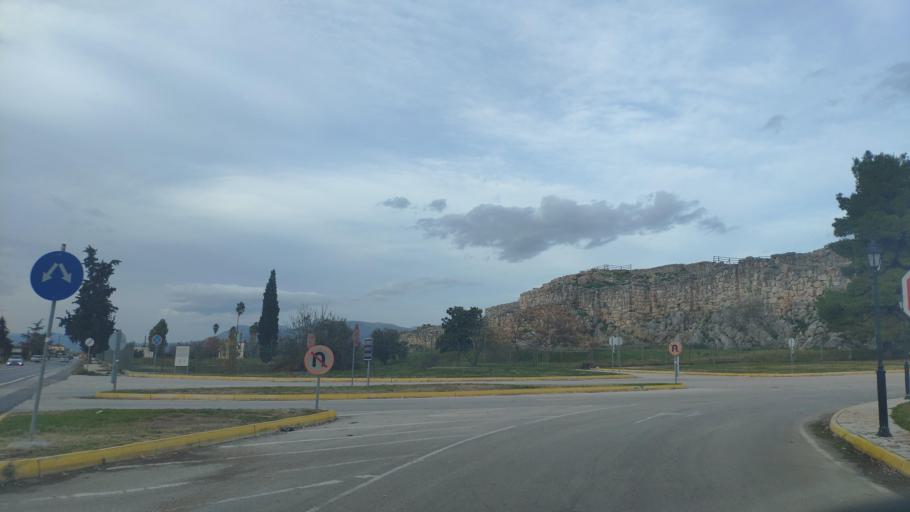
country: GR
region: Peloponnese
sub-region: Nomos Argolidos
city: Nea Tirins
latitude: 37.5973
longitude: 22.7994
